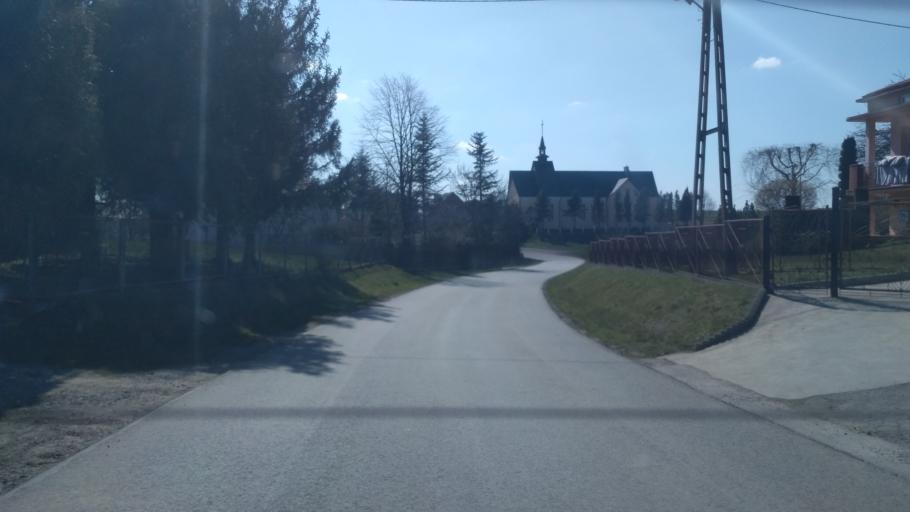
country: PL
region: Subcarpathian Voivodeship
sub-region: Powiat jaroslawski
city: Pawlosiow
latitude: 49.9631
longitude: 22.6469
